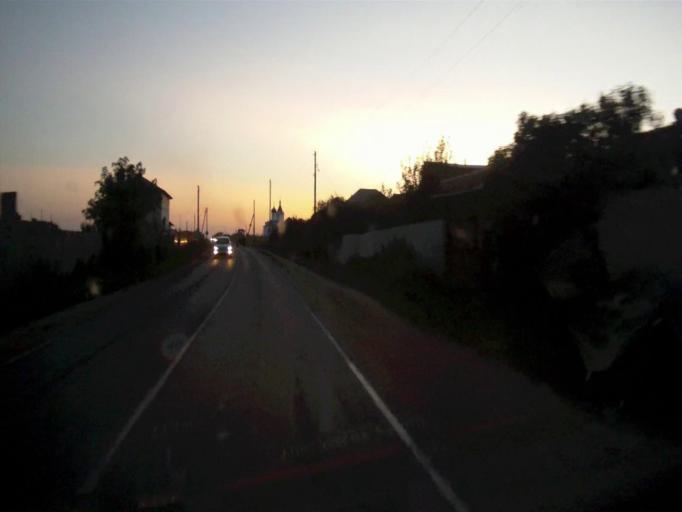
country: RU
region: Chelyabinsk
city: Poletayevo
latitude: 55.2211
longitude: 60.9807
